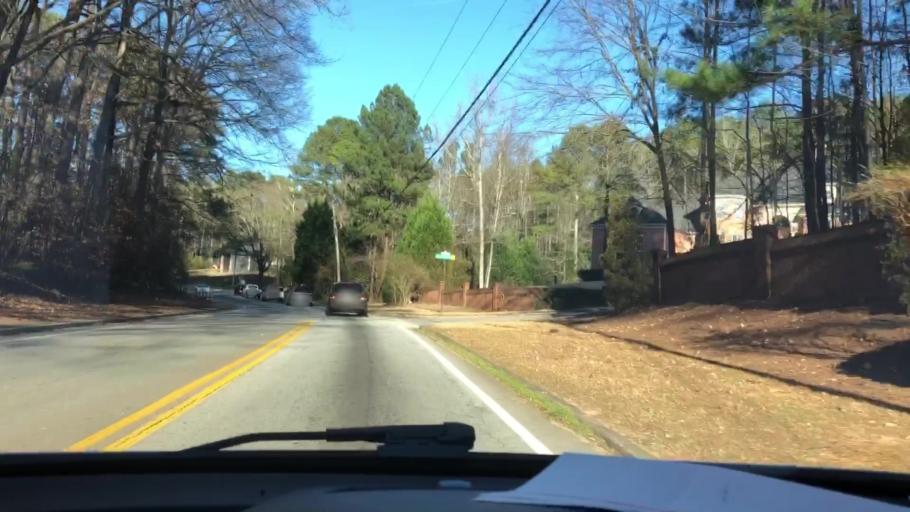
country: US
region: Georgia
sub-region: DeKalb County
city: Stone Mountain
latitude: 33.8289
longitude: -84.1531
